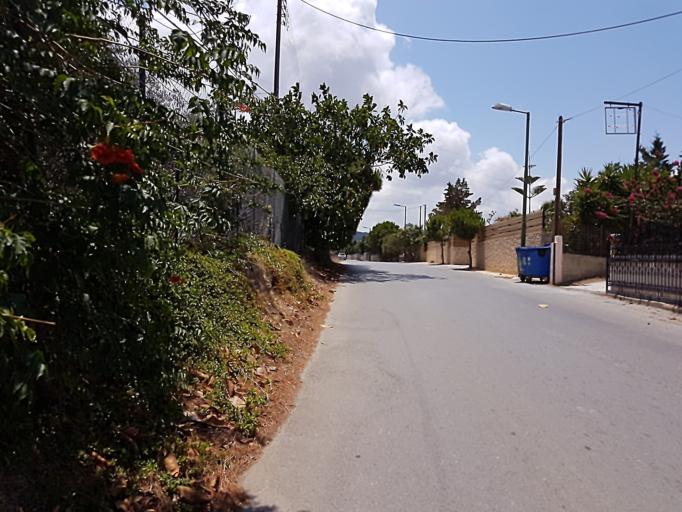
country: GR
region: Crete
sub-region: Nomos Irakleiou
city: Limin Khersonisou
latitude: 35.3149
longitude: 25.3805
